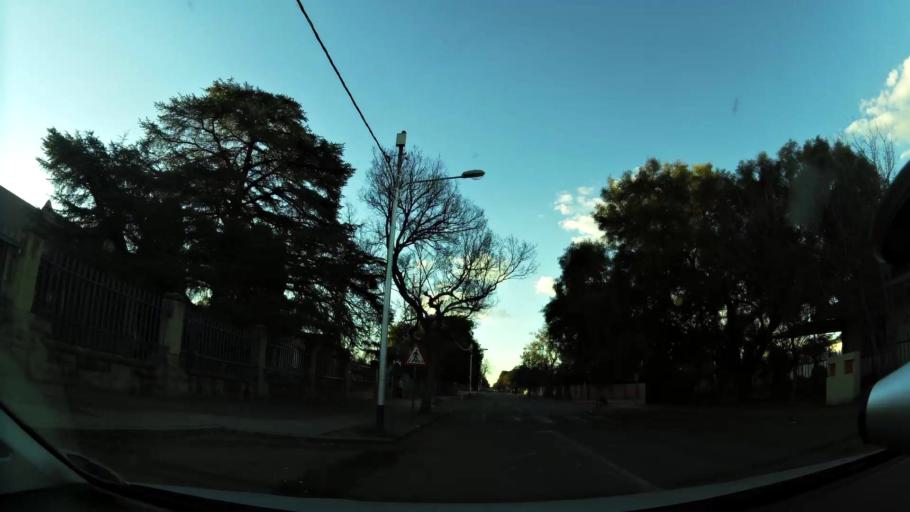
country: ZA
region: North-West
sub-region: Dr Kenneth Kaunda District Municipality
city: Potchefstroom
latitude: -26.7254
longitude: 27.0921
